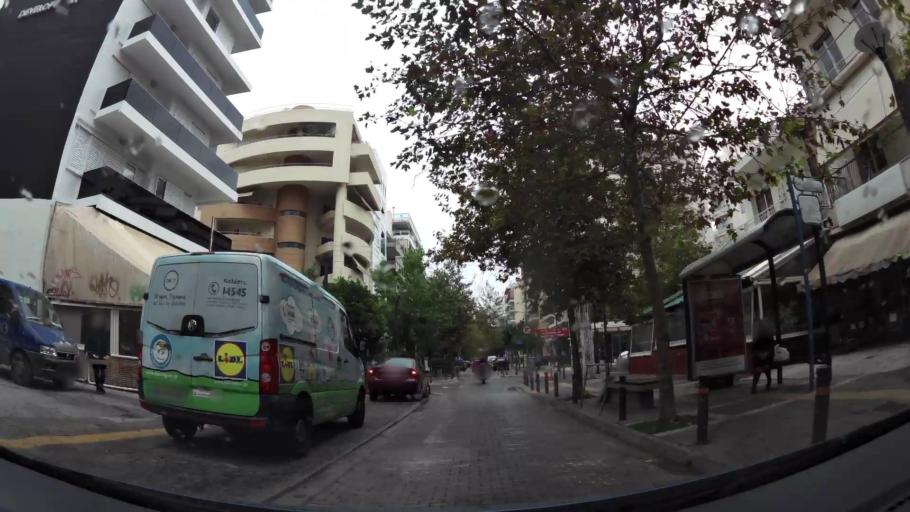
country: GR
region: Attica
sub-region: Nomarchia Athinas
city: Palaio Faliro
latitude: 37.9305
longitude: 23.6951
